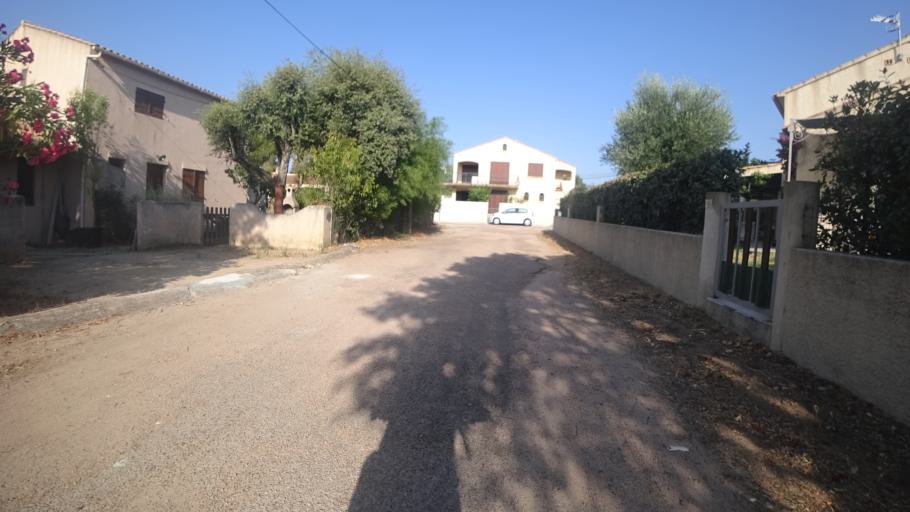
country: FR
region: Corsica
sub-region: Departement de la Corse-du-Sud
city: Porto-Vecchio
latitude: 41.6384
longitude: 9.3408
